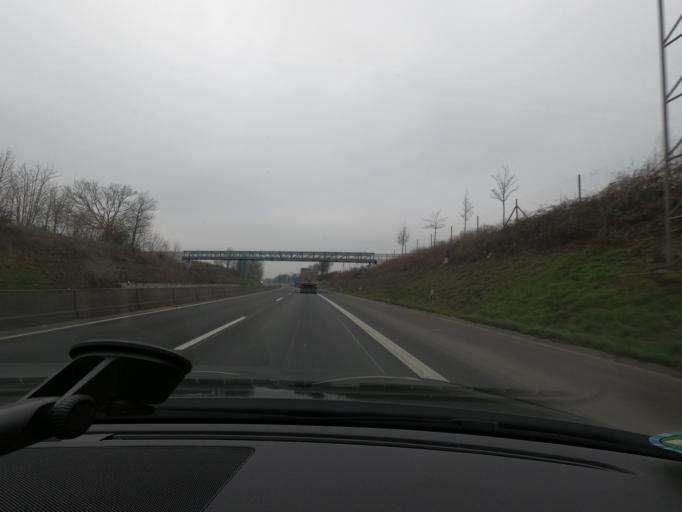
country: DE
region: North Rhine-Westphalia
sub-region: Regierungsbezirk Dusseldorf
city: Nettetal
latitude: 51.3224
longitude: 6.2219
